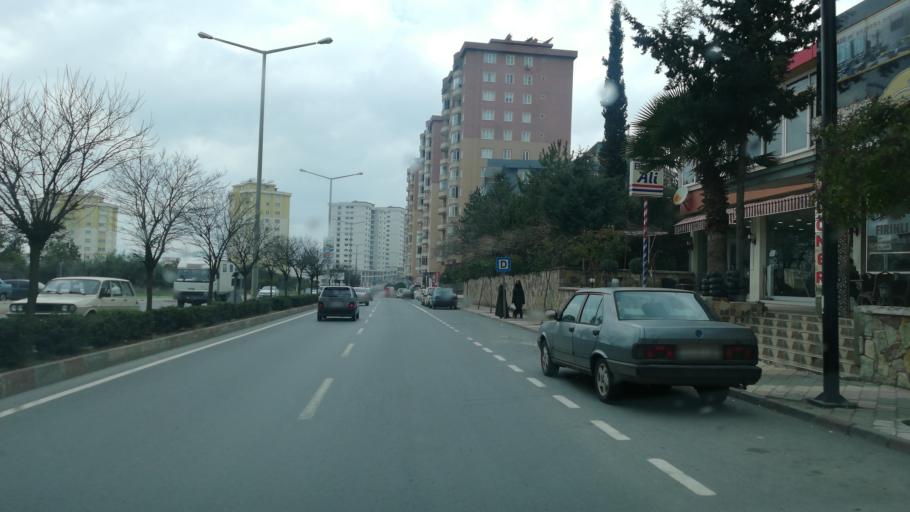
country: TR
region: Kahramanmaras
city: Kahramanmaras
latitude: 37.5847
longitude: 36.8646
